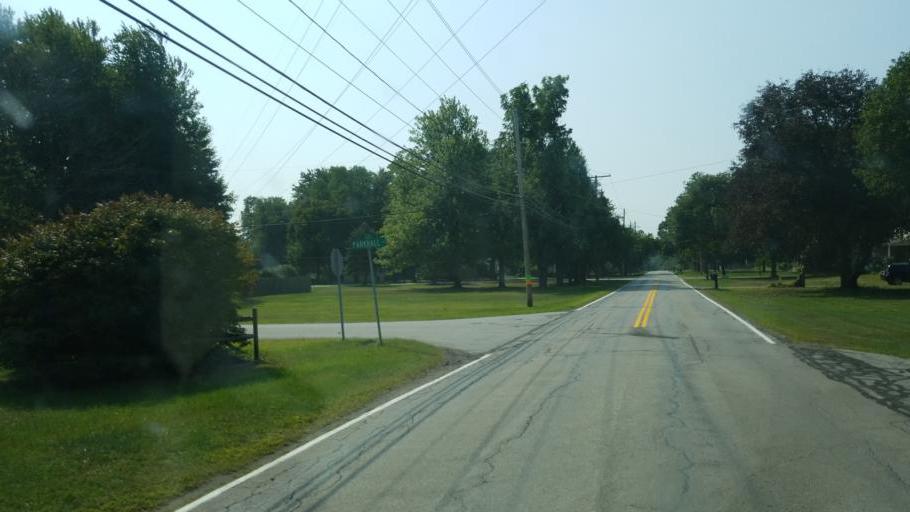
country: US
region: Ohio
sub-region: Lake County
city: Painesville
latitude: 41.7329
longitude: -81.2061
